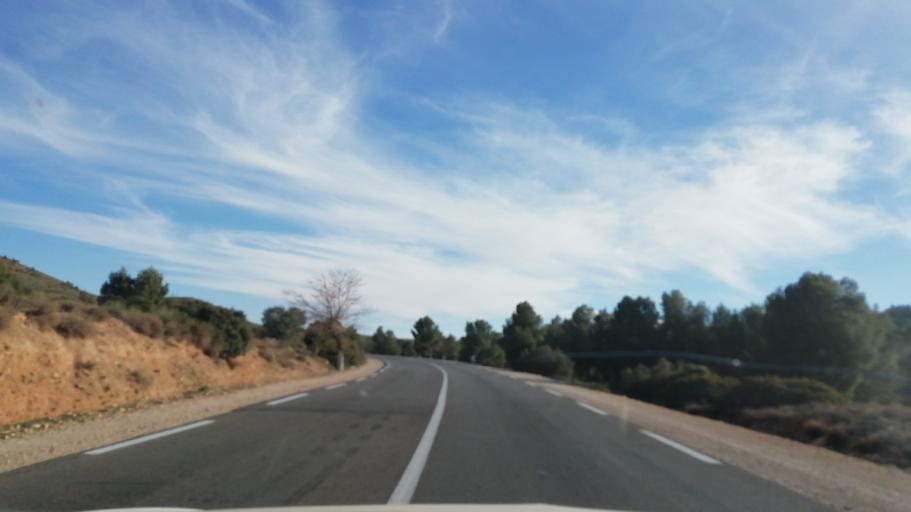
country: DZ
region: Tlemcen
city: Sebdou
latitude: 34.5969
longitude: -1.3231
